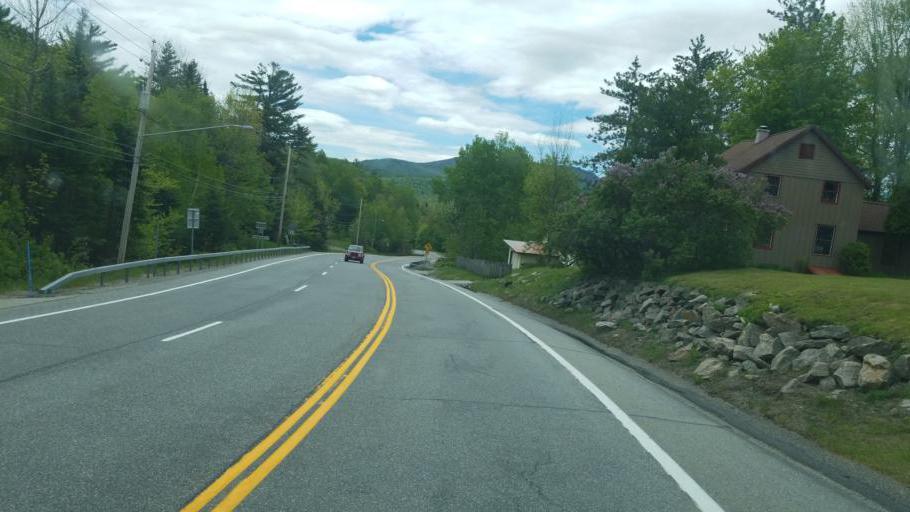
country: US
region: New York
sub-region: Franklin County
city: Tupper Lake
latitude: 43.8691
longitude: -74.4318
